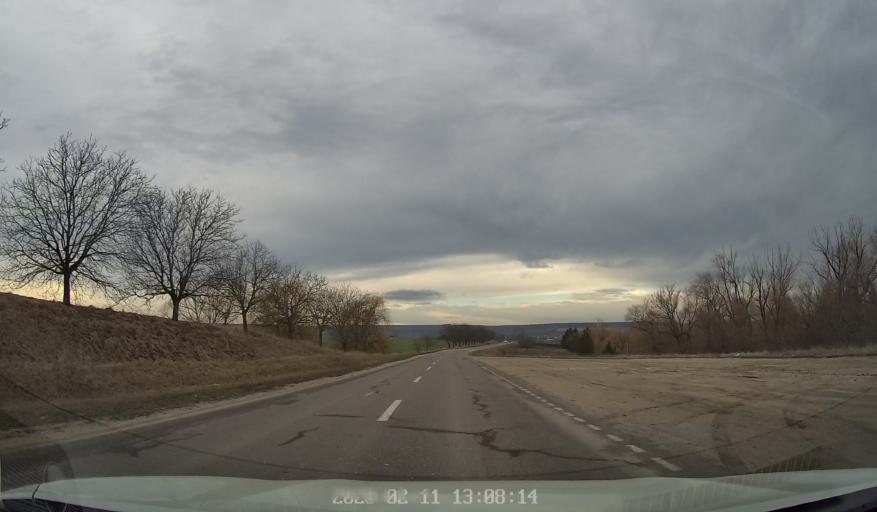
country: RO
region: Botosani
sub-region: Comuna Radauti-Prut
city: Miorcani
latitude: 48.2868
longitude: 26.8915
